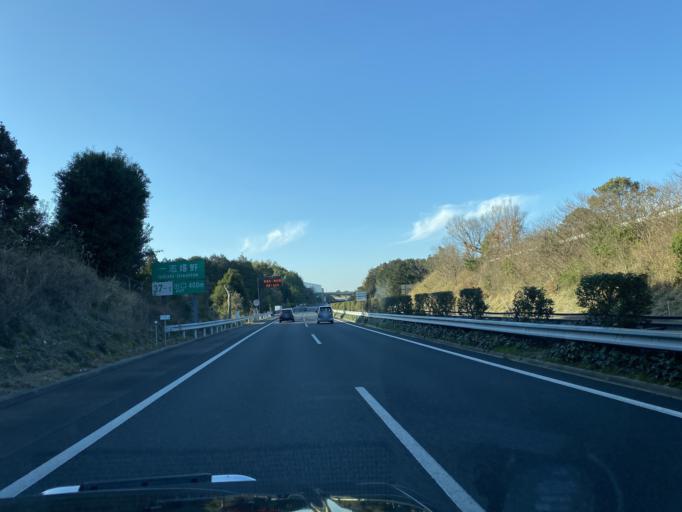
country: JP
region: Mie
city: Hisai-motomachi
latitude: 34.6248
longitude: 136.4531
